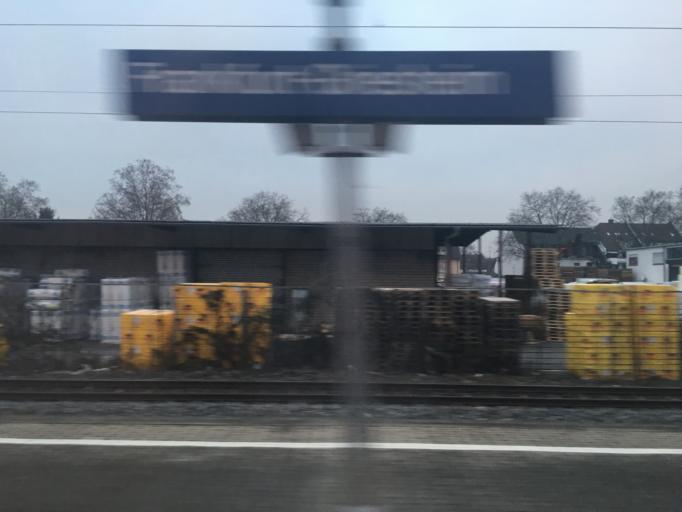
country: DE
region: Hesse
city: Niederrad
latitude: 50.0943
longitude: 8.6047
